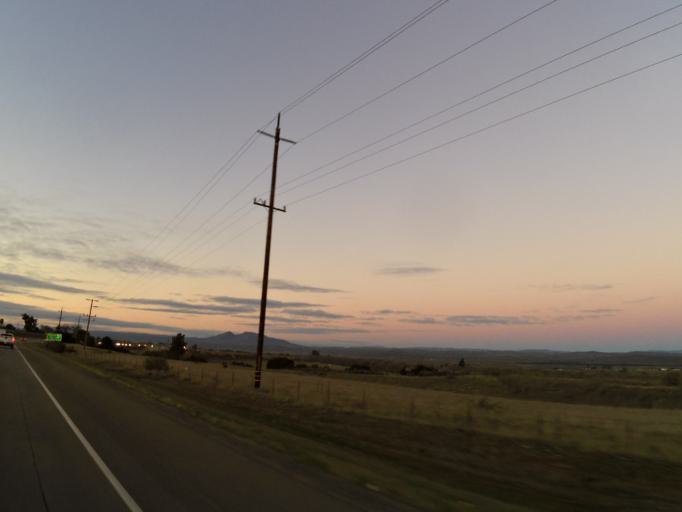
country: US
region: California
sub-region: Monterey County
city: King City
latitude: 36.2270
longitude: -121.1720
